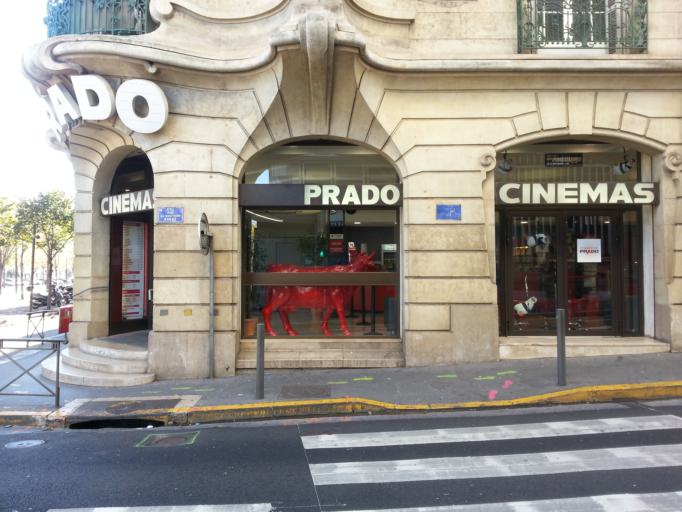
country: FR
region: Provence-Alpes-Cote d'Azur
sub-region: Departement des Bouches-du-Rhone
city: Marseille 06
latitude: 43.2840
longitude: 5.3846
